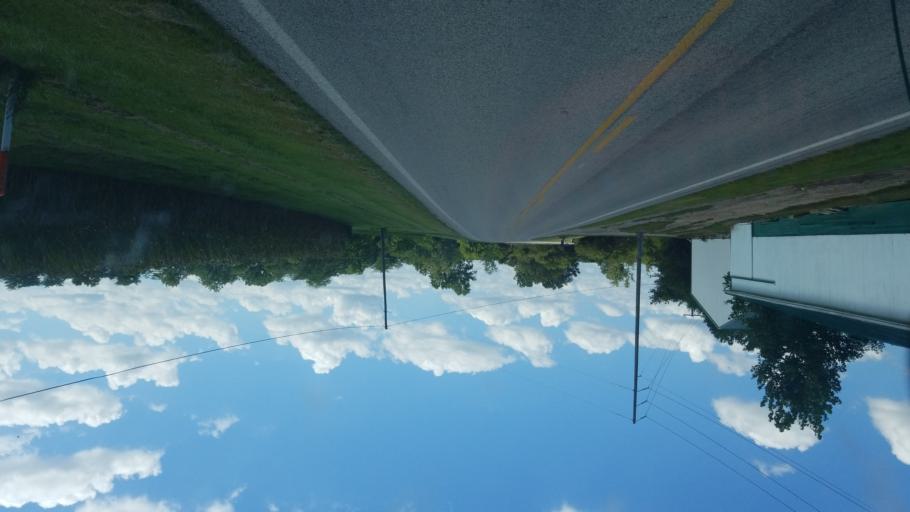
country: US
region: Ohio
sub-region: Marion County
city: Prospect
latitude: 40.3254
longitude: -83.1943
